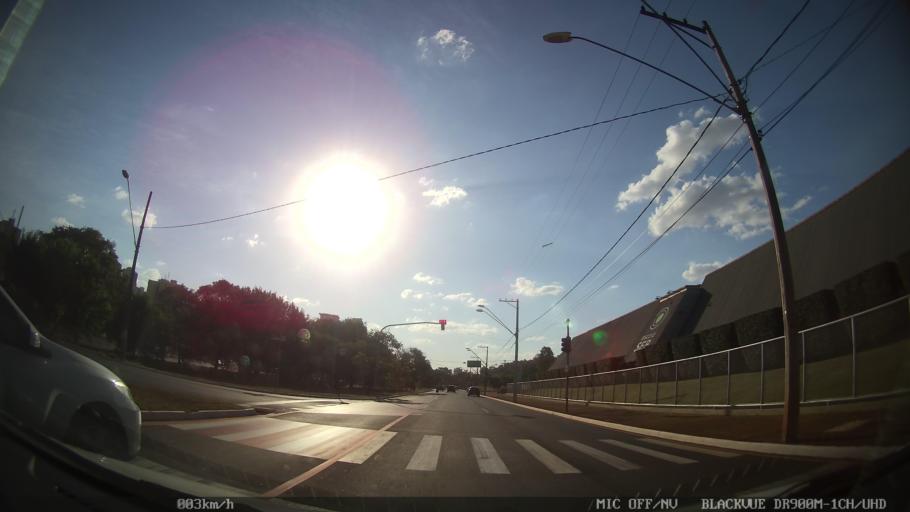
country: BR
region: Sao Paulo
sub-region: Ribeirao Preto
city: Ribeirao Preto
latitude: -21.2042
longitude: -47.7926
